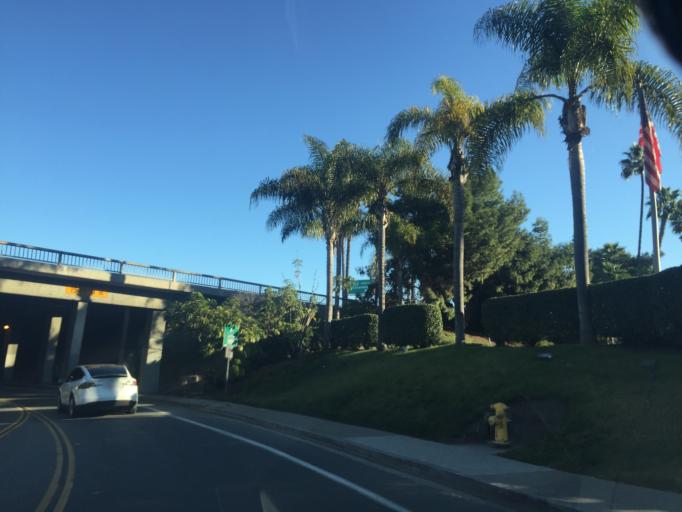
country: US
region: California
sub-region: San Diego County
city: San Diego
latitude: 32.7608
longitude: -117.1665
